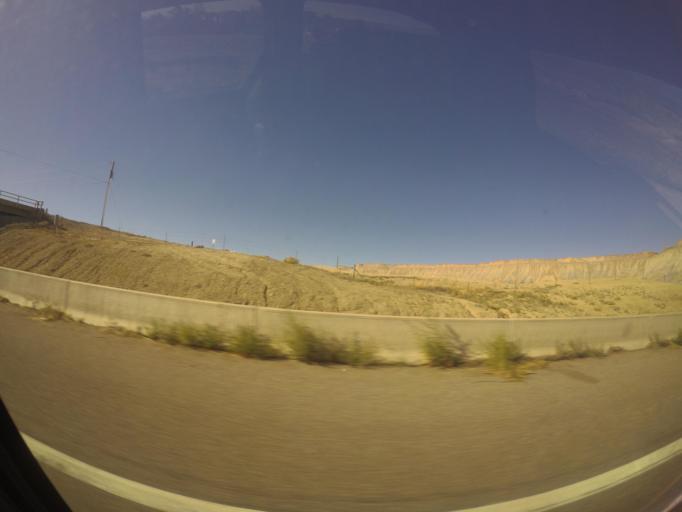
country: US
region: Colorado
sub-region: Mesa County
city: Clifton
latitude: 39.1077
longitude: -108.4403
